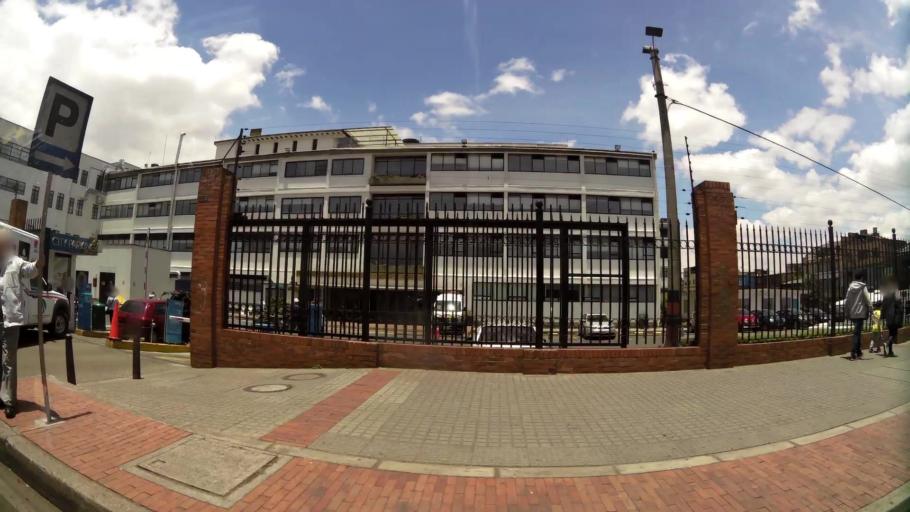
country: CO
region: Bogota D.C.
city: Bogota
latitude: 4.5934
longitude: -74.0878
